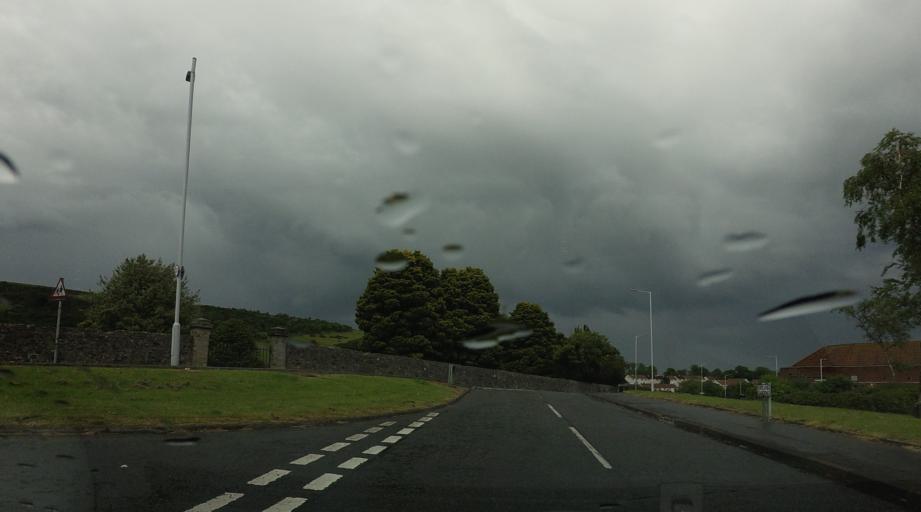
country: GB
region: Scotland
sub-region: Fife
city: Ballingry
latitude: 56.1644
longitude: -3.3270
